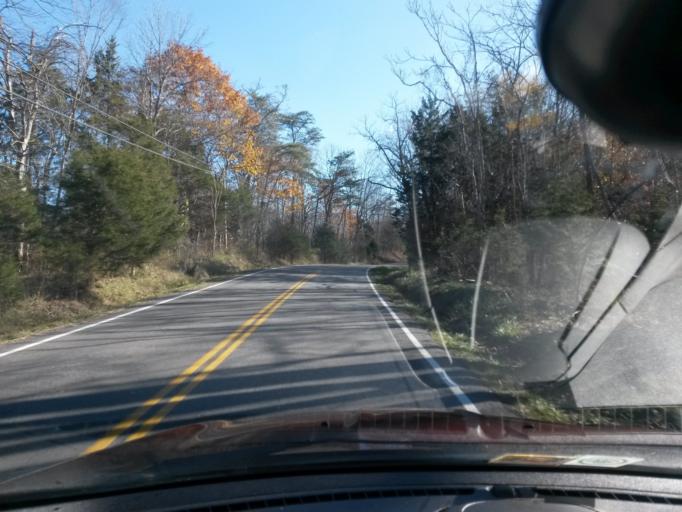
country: US
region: Virginia
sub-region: Botetourt County
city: Buchanan
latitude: 37.6435
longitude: -79.7675
